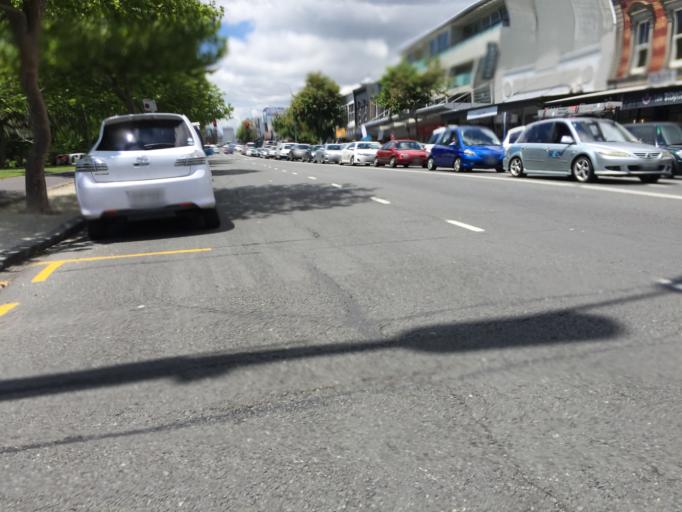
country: NZ
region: Auckland
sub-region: Auckland
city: Auckland
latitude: -36.8577
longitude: 174.7494
